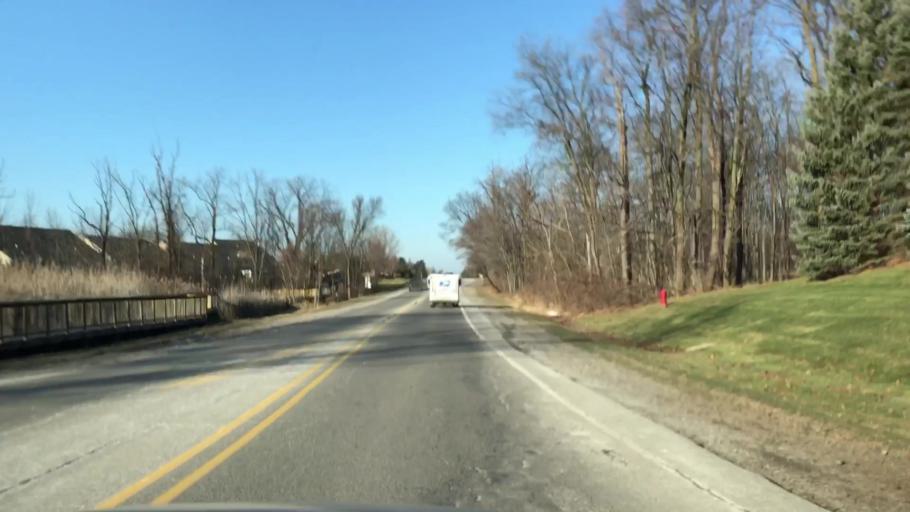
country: US
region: Michigan
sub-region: Oakland County
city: Novi
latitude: 42.4724
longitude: -83.5146
